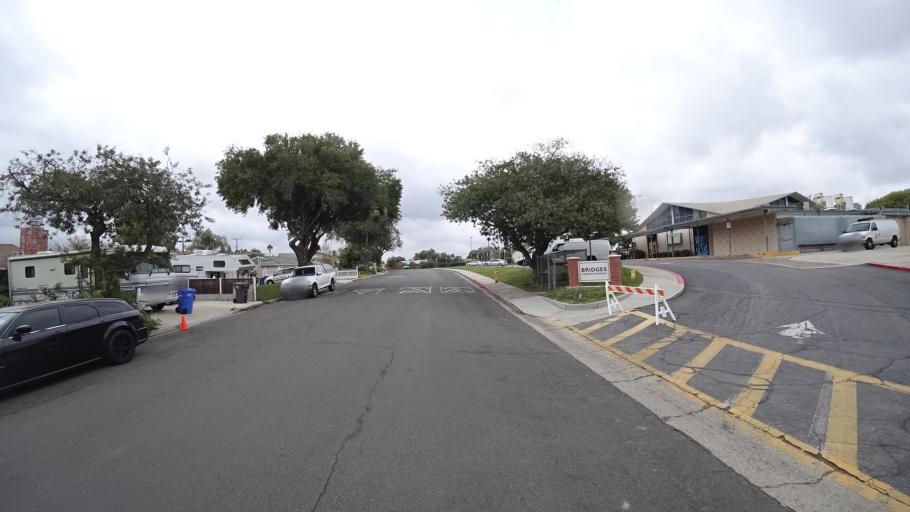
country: US
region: California
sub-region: Ventura County
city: Thousand Oaks
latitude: 34.2118
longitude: -118.8555
